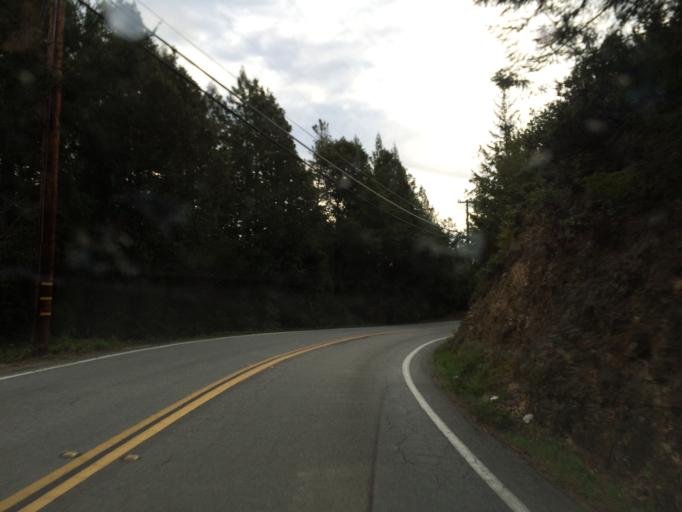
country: US
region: California
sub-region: Santa Cruz County
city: Bonny Doon
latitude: 37.0535
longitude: -122.1158
